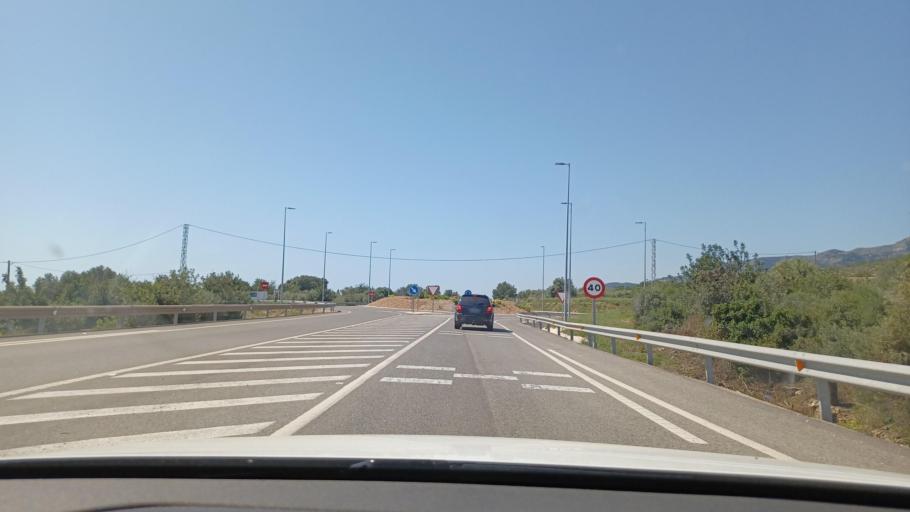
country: ES
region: Catalonia
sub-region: Provincia de Tarragona
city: Sant Carles de la Rapita
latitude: 40.6233
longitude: 0.5770
